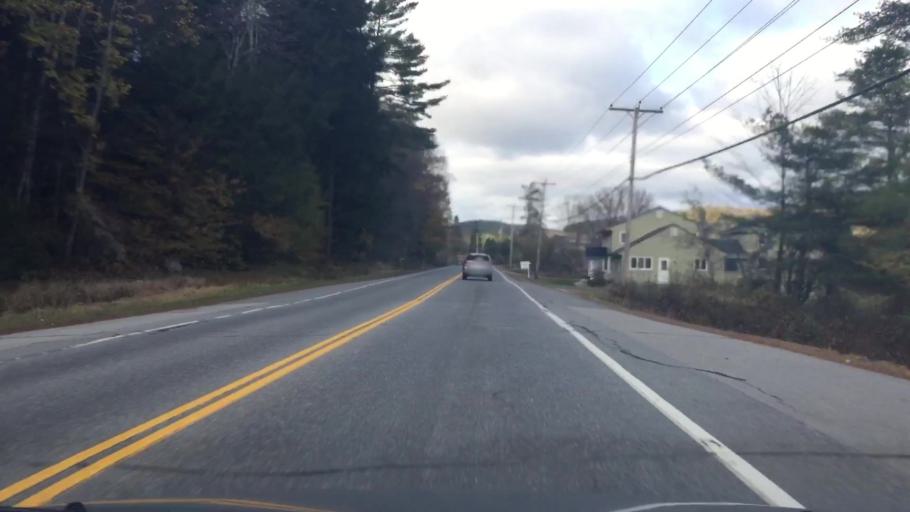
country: US
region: New Hampshire
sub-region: Cheshire County
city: Keene
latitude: 43.0002
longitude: -72.2589
